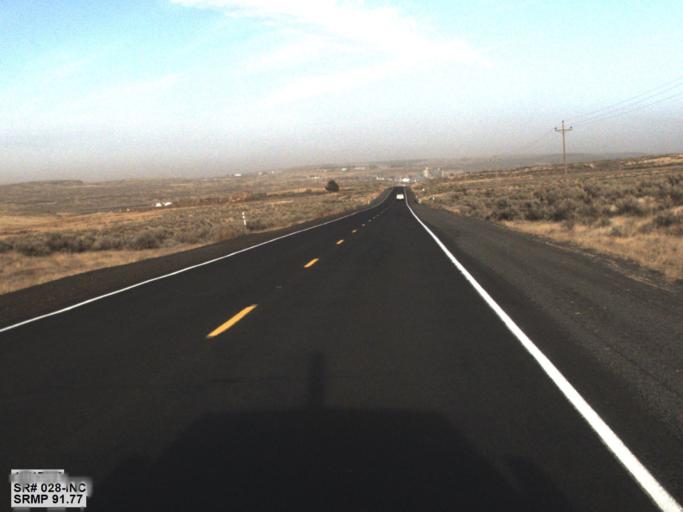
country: US
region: Washington
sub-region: Adams County
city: Ritzville
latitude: 47.3220
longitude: -118.7297
